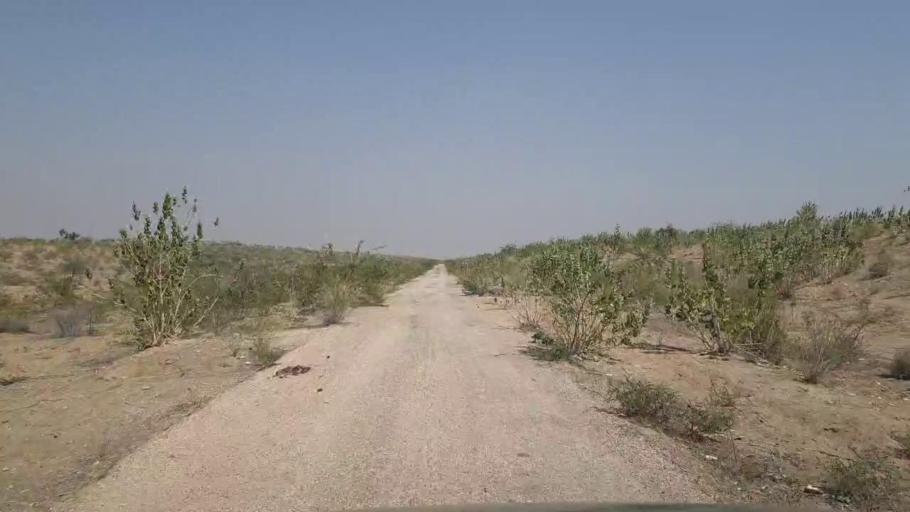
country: PK
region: Sindh
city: Chor
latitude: 25.5815
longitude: 70.1941
